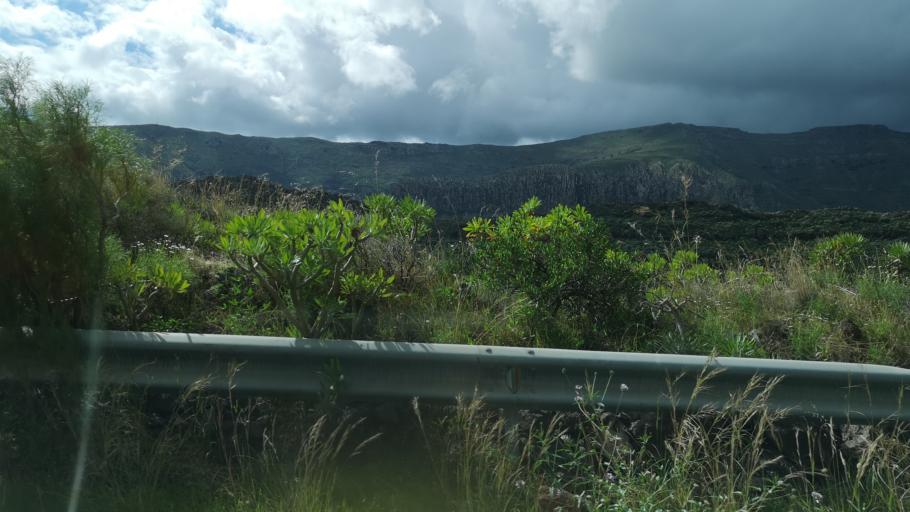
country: ES
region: Canary Islands
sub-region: Provincia de Santa Cruz de Tenerife
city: San Sebastian de la Gomera
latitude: 28.1133
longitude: -17.1356
